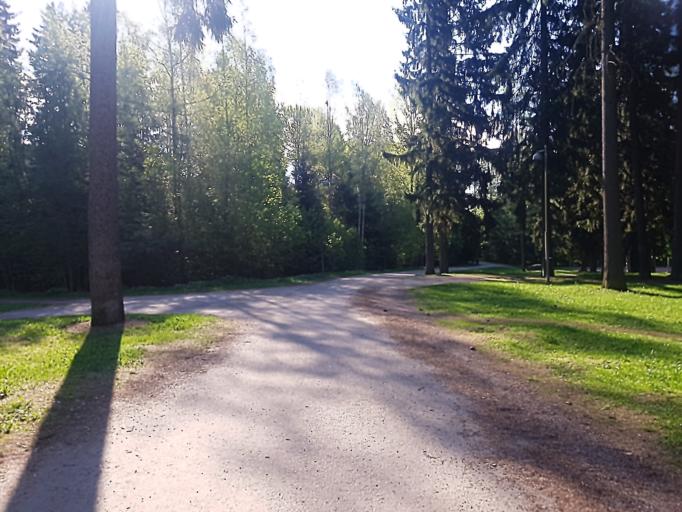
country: FI
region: Uusimaa
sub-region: Helsinki
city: Helsinki
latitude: 60.2321
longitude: 24.9289
